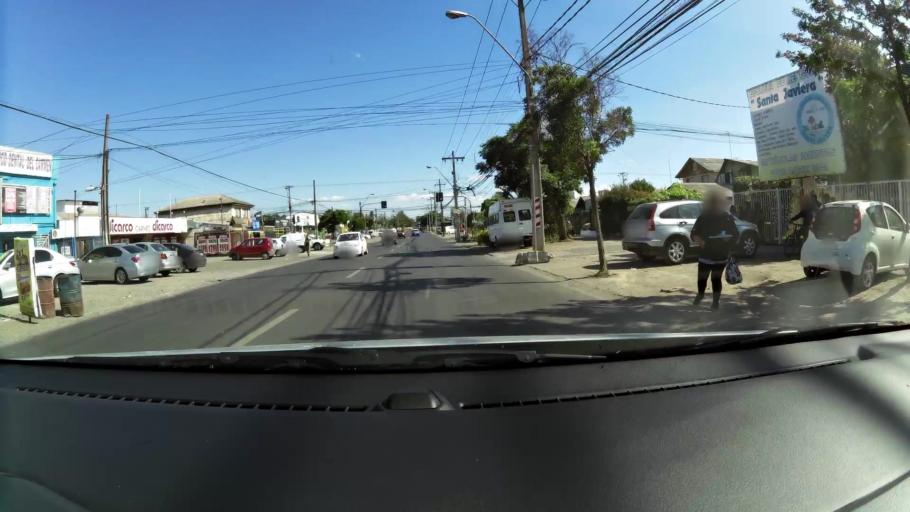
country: CL
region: Santiago Metropolitan
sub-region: Provincia de Santiago
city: Lo Prado
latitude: -33.5115
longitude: -70.7756
